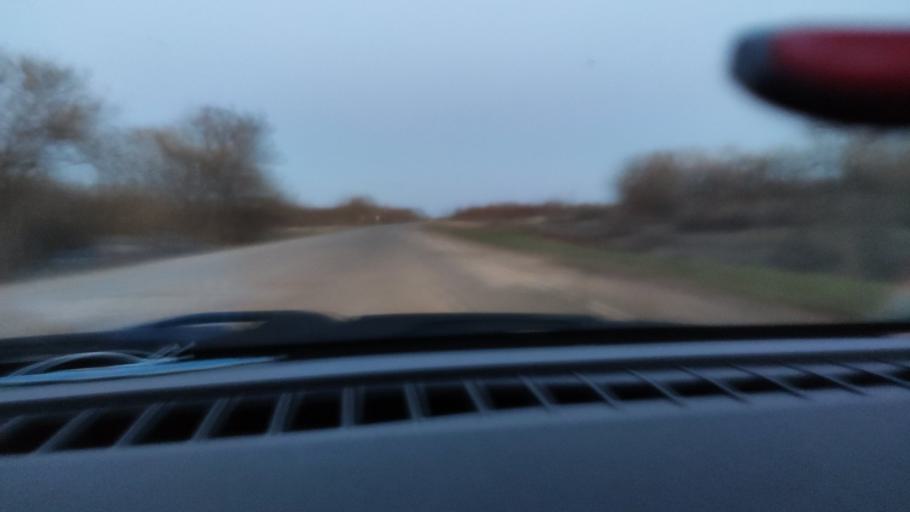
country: RU
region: Saratov
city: Rovnoye
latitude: 51.0384
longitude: 46.0747
